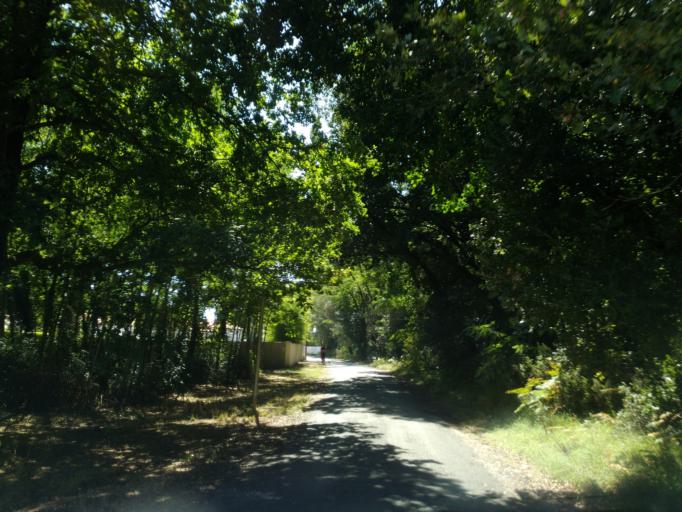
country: FR
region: Poitou-Charentes
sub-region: Departement de la Charente-Maritime
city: Saint-Palais-sur-Mer
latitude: 45.6606
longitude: -1.0762
